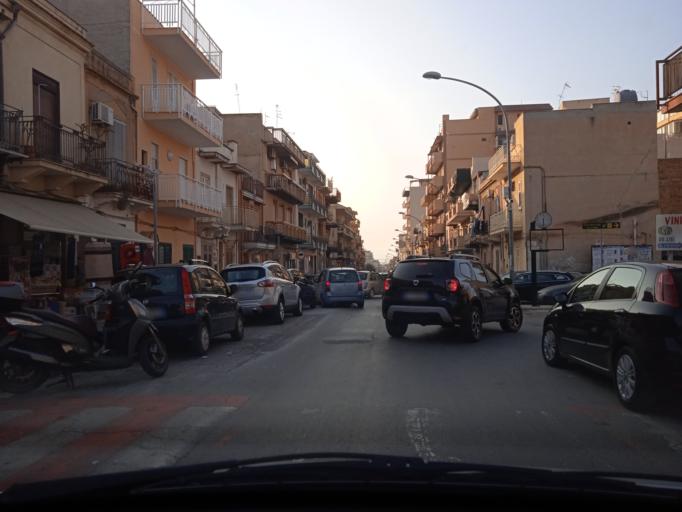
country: IT
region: Sicily
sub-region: Palermo
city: Villabate
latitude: 38.0756
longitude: 13.4493
